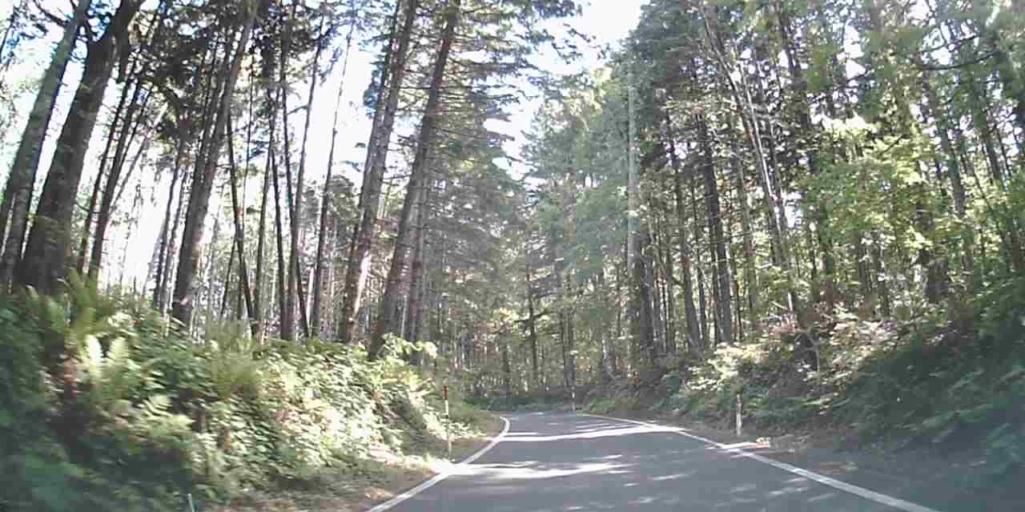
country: JP
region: Hokkaido
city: Shiraoi
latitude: 42.7404
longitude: 141.4106
